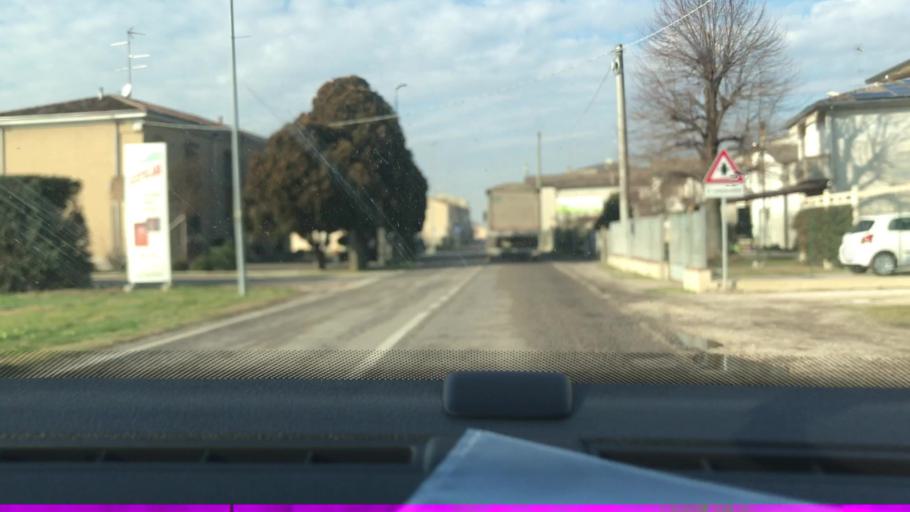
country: IT
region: Veneto
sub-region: Provincia di Rovigo
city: Castelnovo Bariano
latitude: 45.0120
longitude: 11.2700
